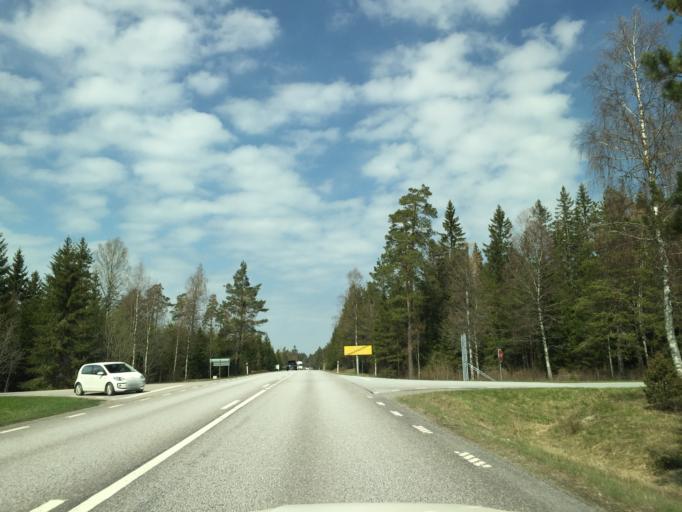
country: SE
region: Vaestra Goetaland
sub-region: Bengtsfors Kommun
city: Dals Langed
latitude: 58.8116
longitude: 12.1463
